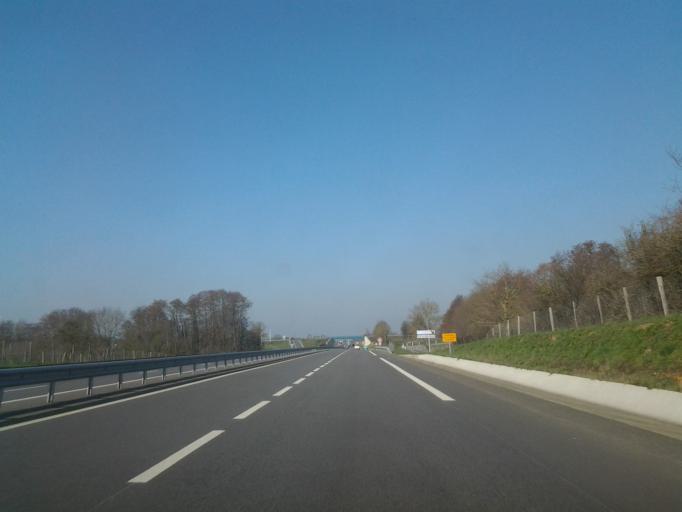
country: FR
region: Pays de la Loire
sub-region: Departement de la Vendee
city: Saint-Christophe-du-Ligneron
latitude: 46.8305
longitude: -1.8116
